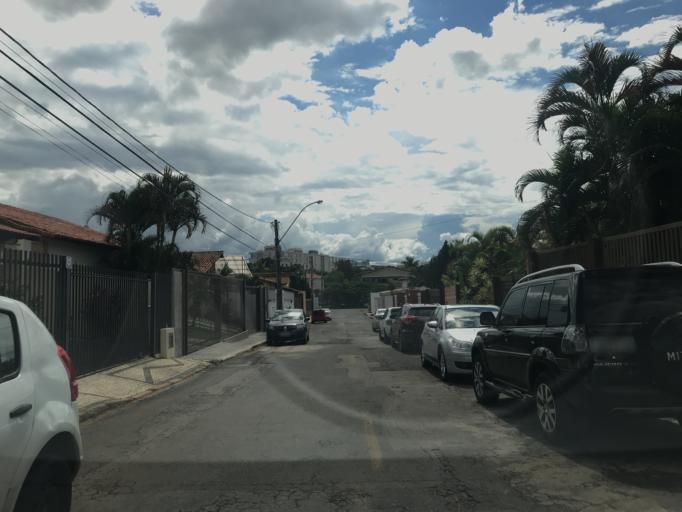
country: BR
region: Federal District
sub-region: Brasilia
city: Brasilia
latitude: -15.7216
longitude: -47.8780
